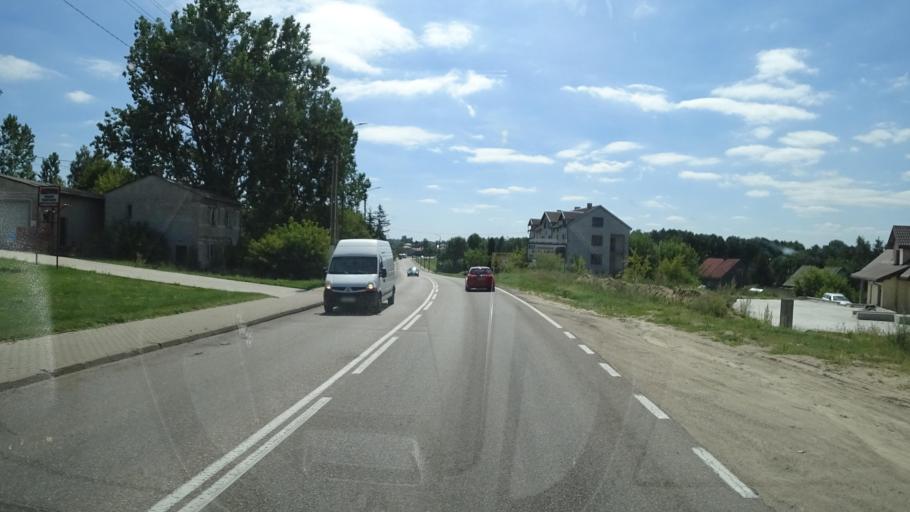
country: PL
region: Podlasie
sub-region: Powiat grajewski
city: Grajewo
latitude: 53.6595
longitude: 22.4540
